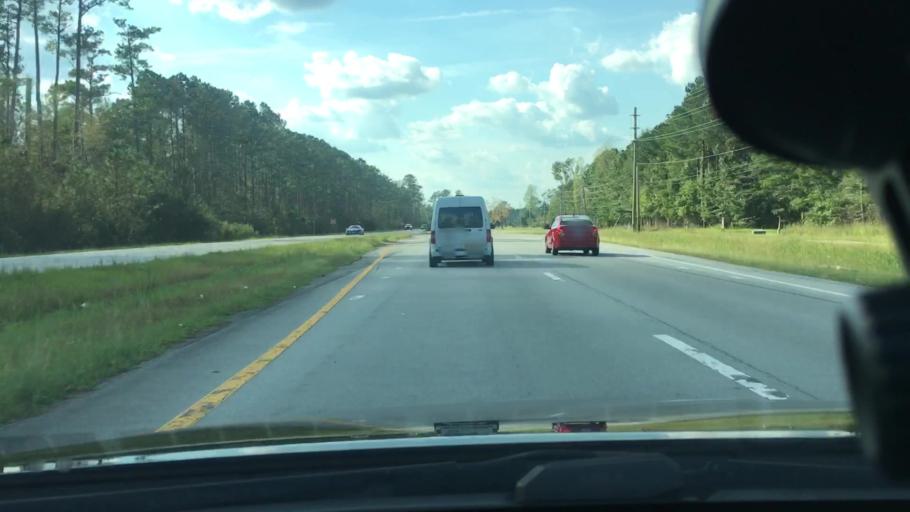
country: US
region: North Carolina
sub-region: Craven County
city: Neuse Forest
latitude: 34.9659
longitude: -76.9626
